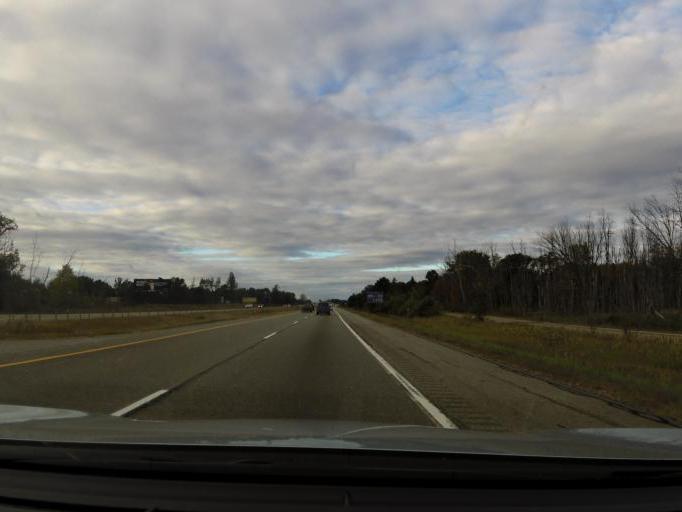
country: US
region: Michigan
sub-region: Livingston County
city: Brighton
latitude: 42.6209
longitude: -83.7488
